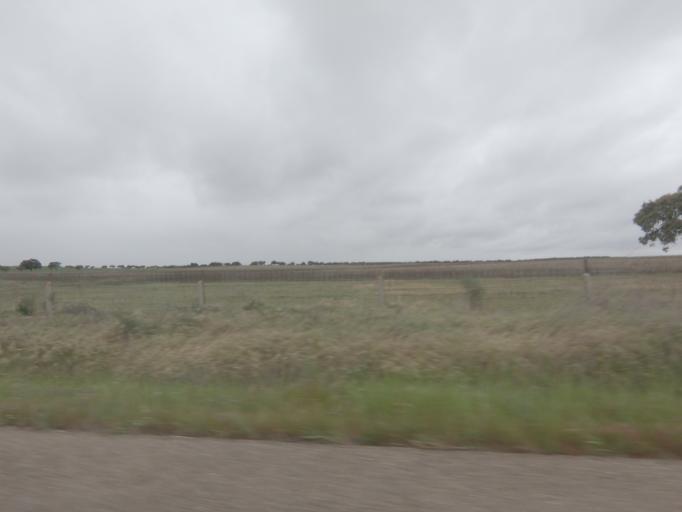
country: ES
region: Extremadura
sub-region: Provincia de Badajoz
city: Badajoz
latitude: 38.9669
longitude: -6.8969
